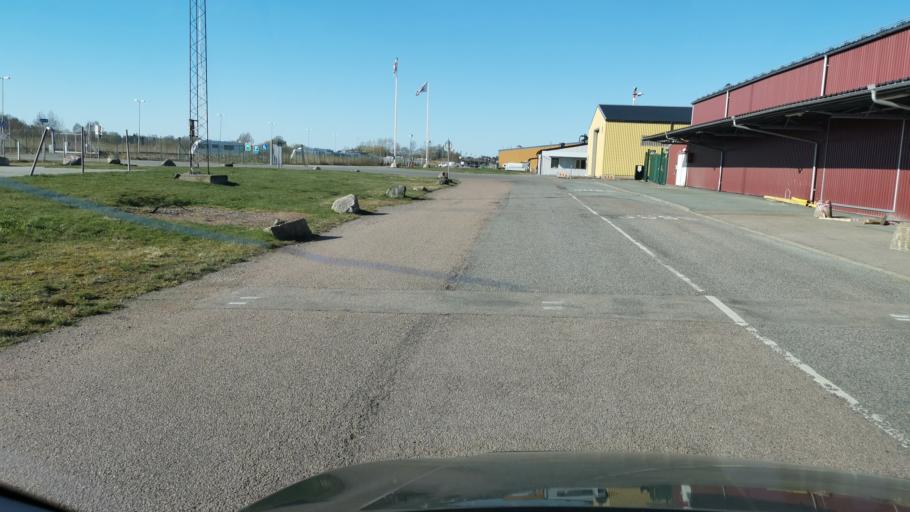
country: SE
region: Vaestra Goetaland
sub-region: Goteborg
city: Majorna
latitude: 57.7777
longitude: 11.8644
